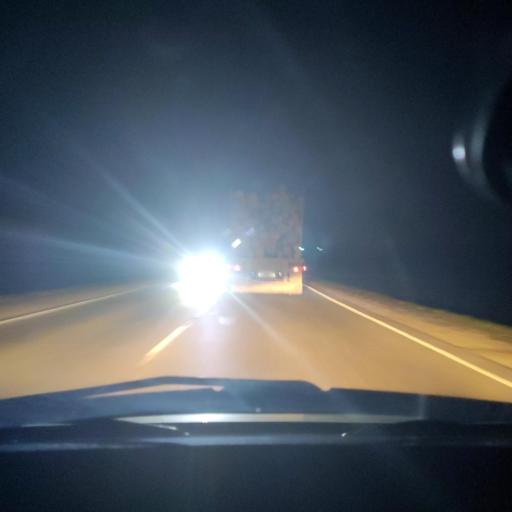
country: RU
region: Bashkortostan
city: Iglino
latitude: 54.8944
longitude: 56.4733
